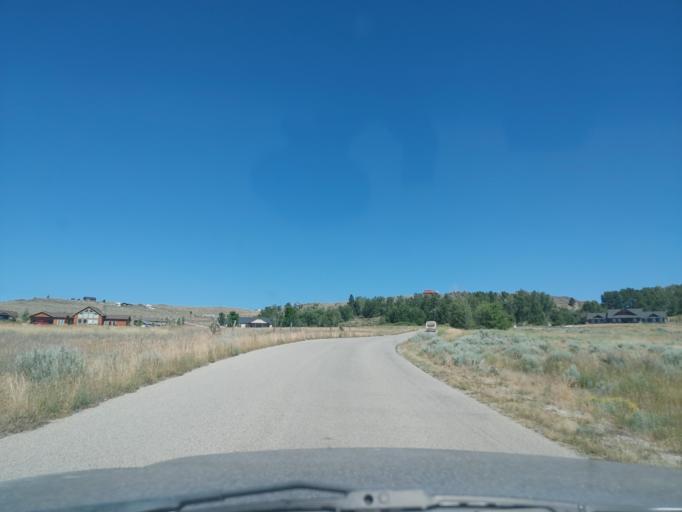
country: US
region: Montana
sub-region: Ravalli County
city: Hamilton
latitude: 46.3484
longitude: -114.0591
